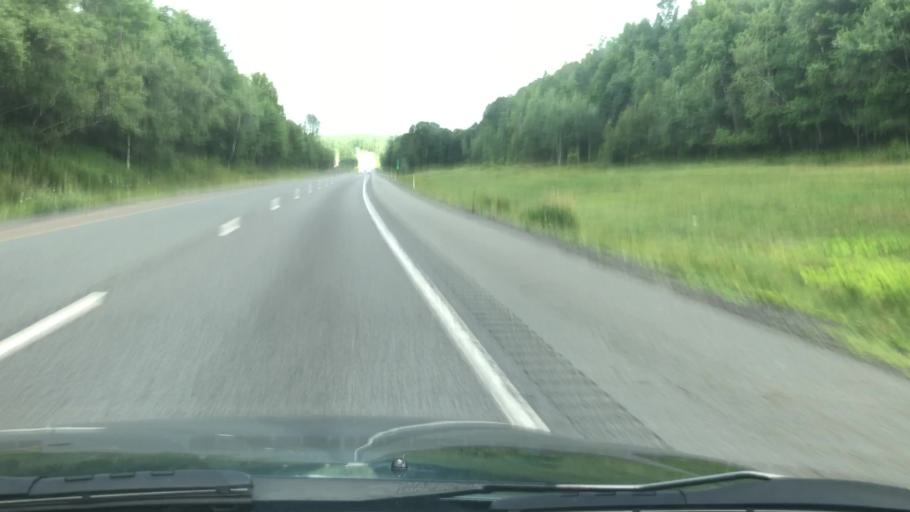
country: US
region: Pennsylvania
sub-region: Pike County
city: Gold Key Lake
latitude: 41.3467
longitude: -74.9311
